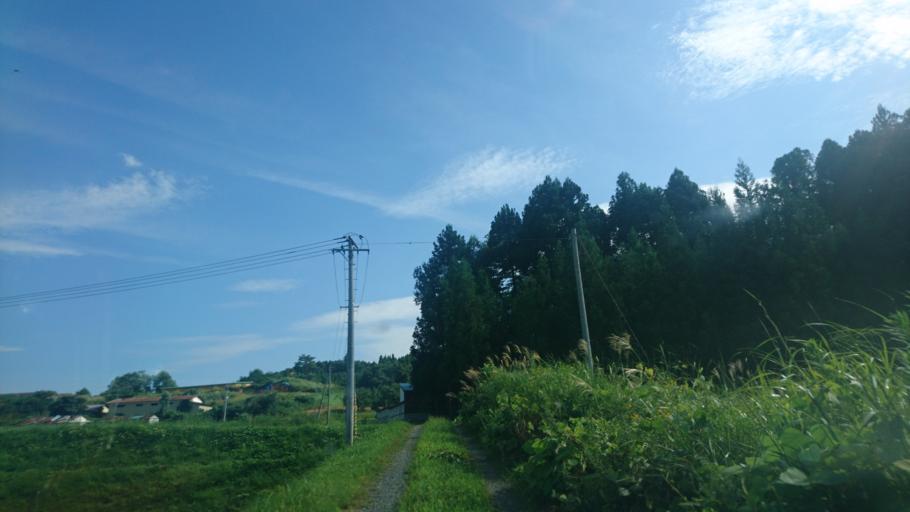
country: JP
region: Miyagi
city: Furukawa
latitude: 38.7664
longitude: 140.9561
